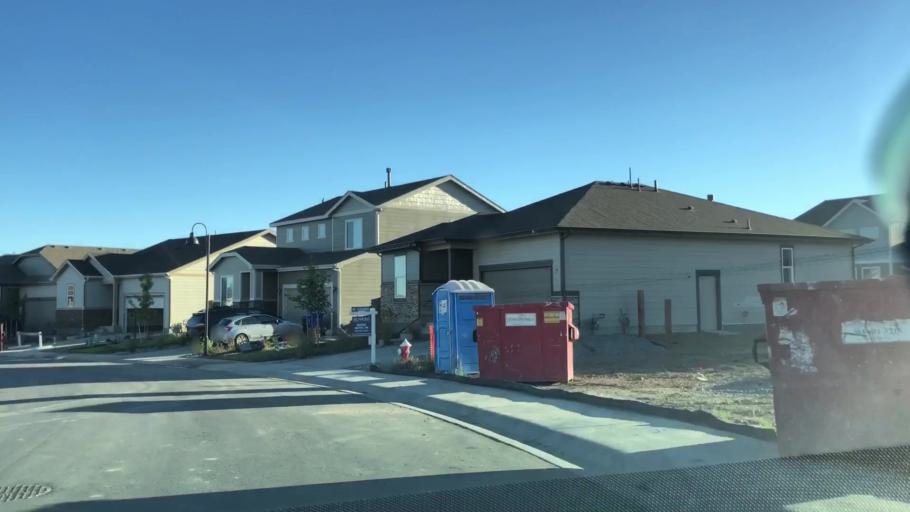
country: US
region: Colorado
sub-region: Larimer County
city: Loveland
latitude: 40.4193
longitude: -105.0185
